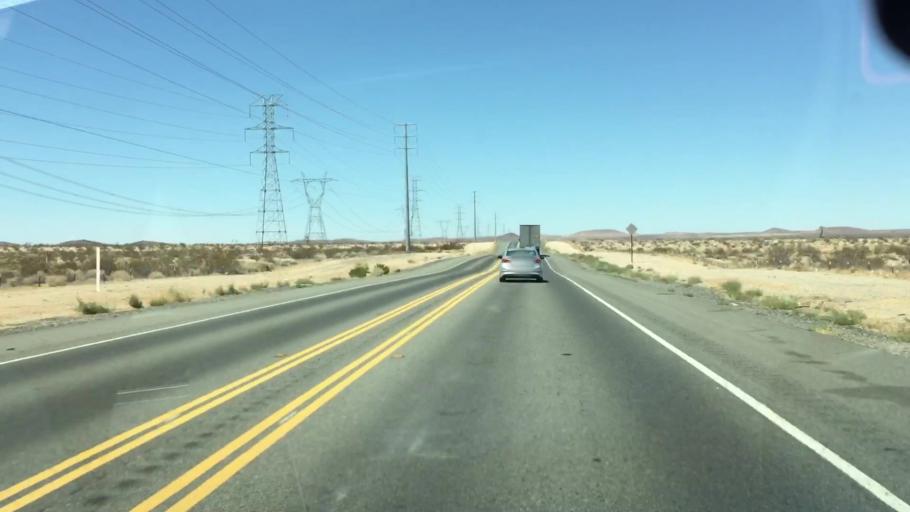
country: US
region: California
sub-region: San Bernardino County
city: Adelanto
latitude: 34.7891
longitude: -117.4831
